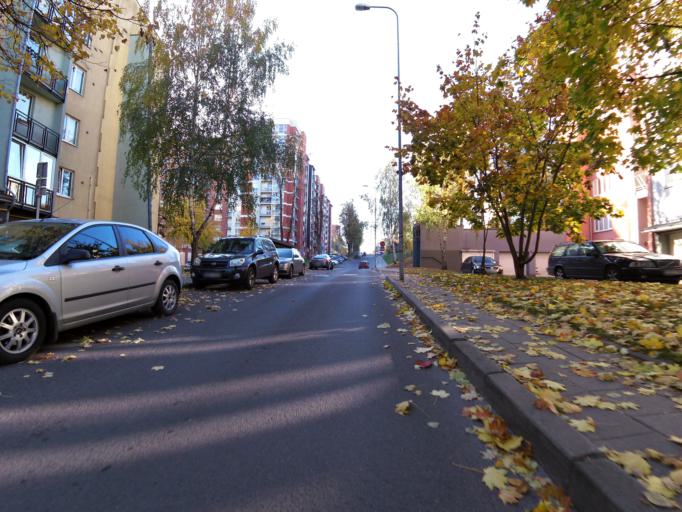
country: LT
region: Vilnius County
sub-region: Vilnius
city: Fabijoniskes
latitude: 54.7412
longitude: 25.2730
